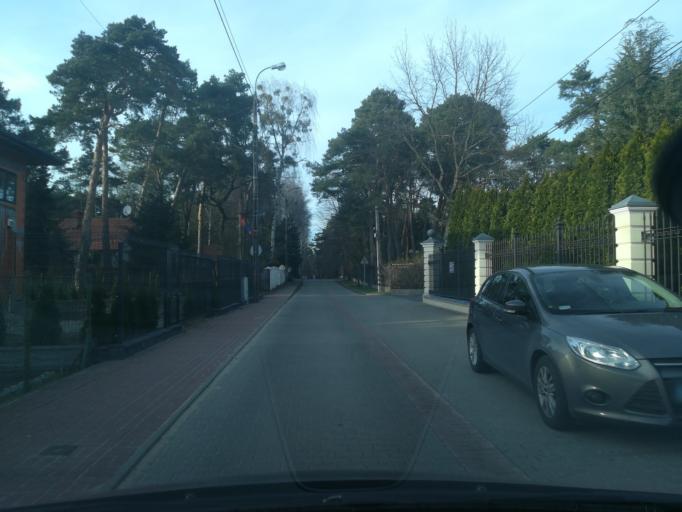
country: PL
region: Masovian Voivodeship
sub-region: Powiat piaseczynski
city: Konstancin-Jeziorna
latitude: 52.0714
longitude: 21.1048
